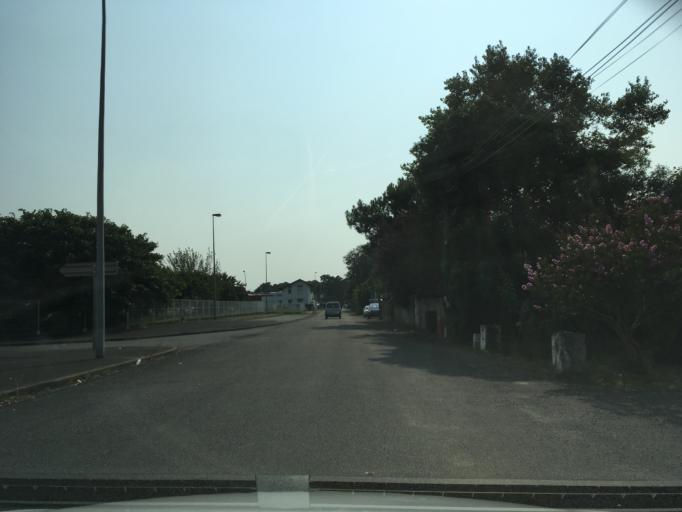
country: FR
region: Aquitaine
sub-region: Departement des Pyrenees-Atlantiques
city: Boucau
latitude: 43.5236
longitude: -1.5001
